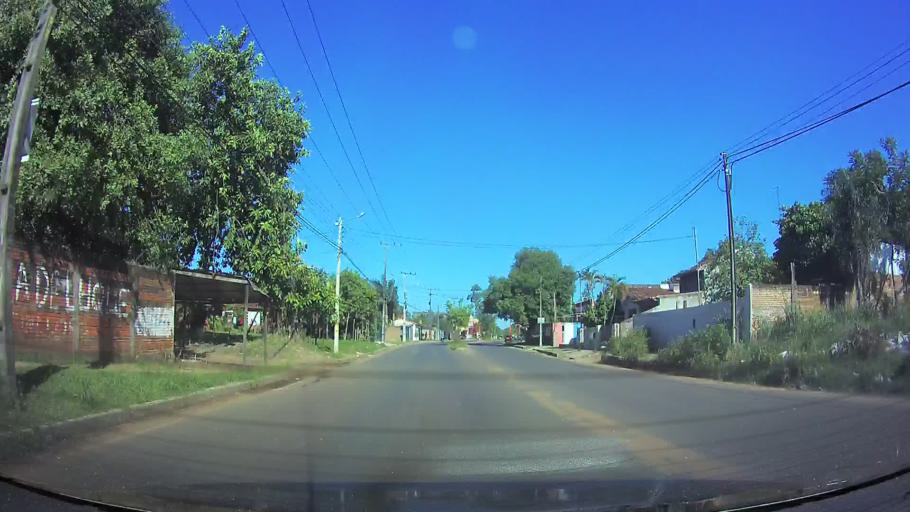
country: PY
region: Central
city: San Lorenzo
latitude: -25.2981
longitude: -57.5101
